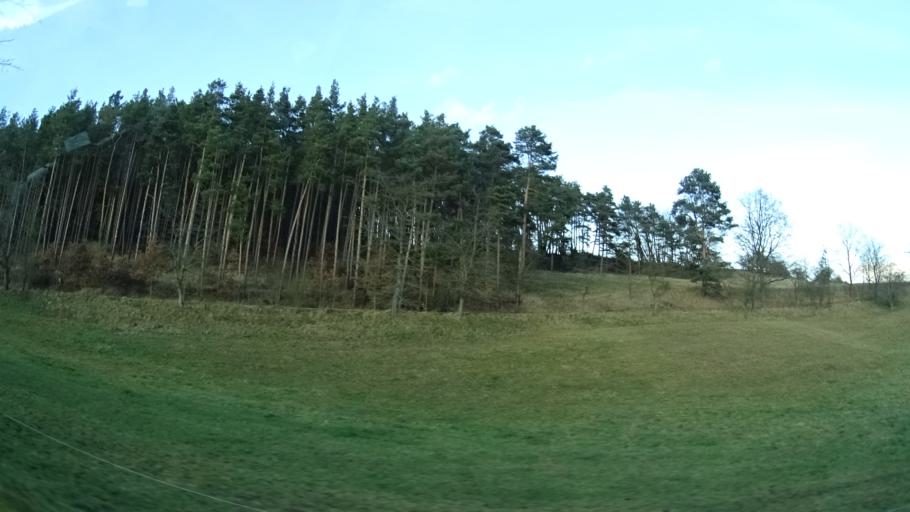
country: DE
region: Thuringia
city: Rudolstadt
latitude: 50.7605
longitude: 11.3480
